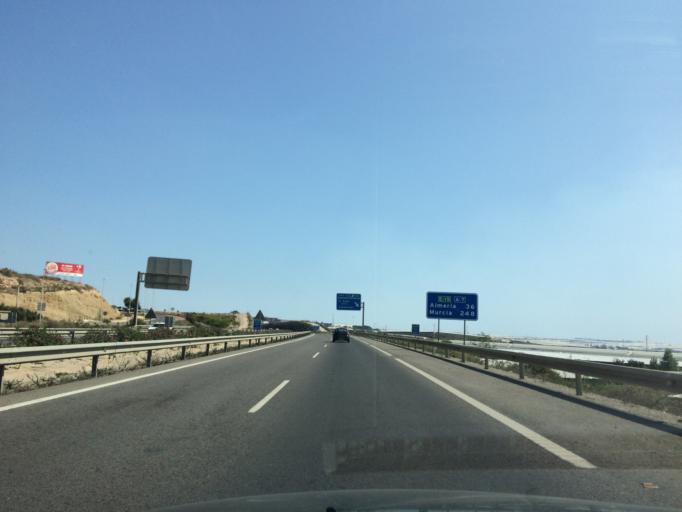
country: ES
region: Andalusia
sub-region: Provincia de Almeria
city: El Ejido
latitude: 36.7628
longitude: -2.8226
